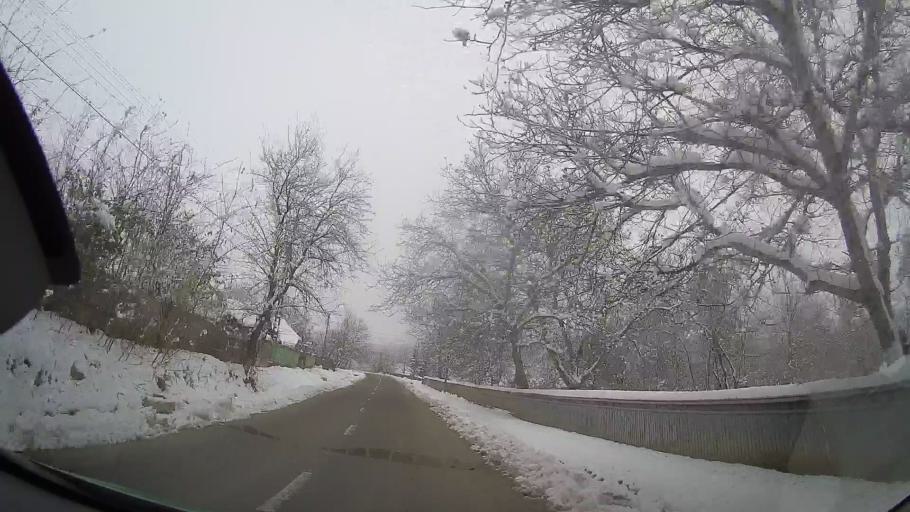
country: RO
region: Neamt
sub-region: Comuna Bozieni
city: Bozieni
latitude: 46.8388
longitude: 27.1501
